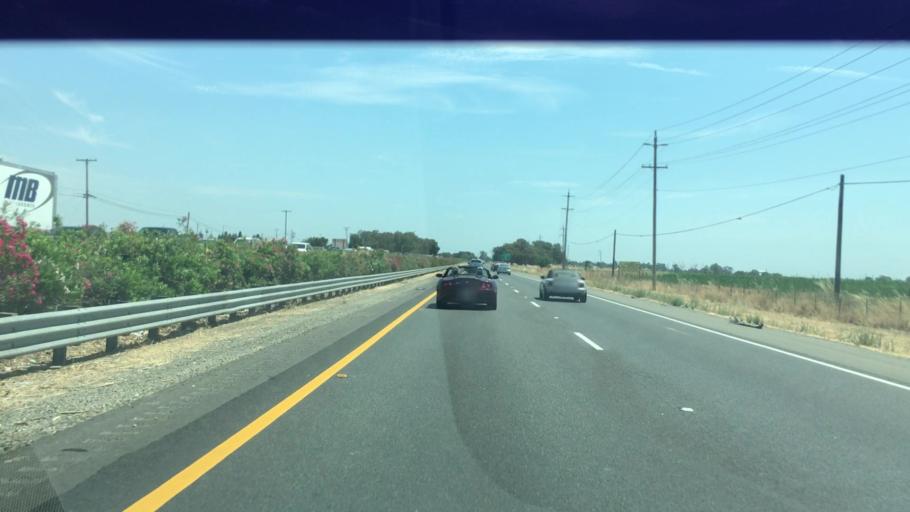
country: US
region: California
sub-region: Sacramento County
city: Galt
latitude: 38.3076
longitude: -121.3201
